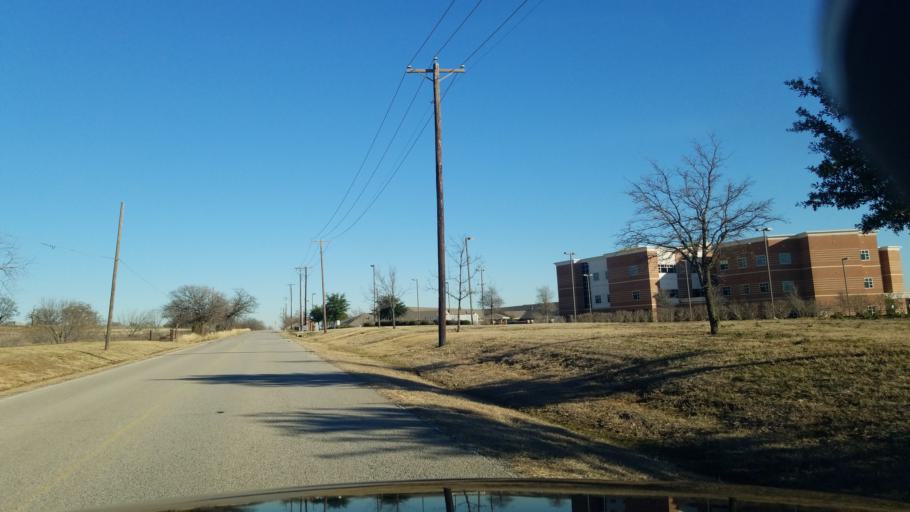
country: US
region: Texas
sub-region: Denton County
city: Corinth
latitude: 33.1545
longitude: -97.0581
